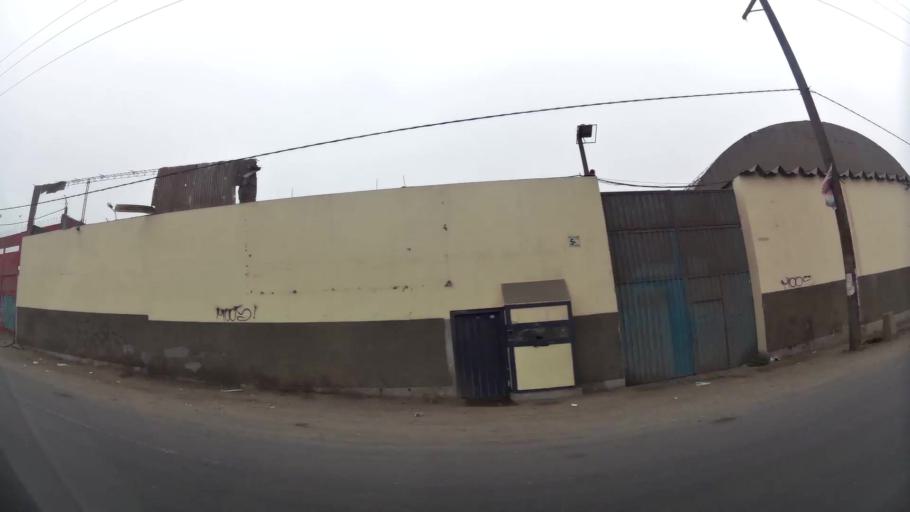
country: PE
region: Lima
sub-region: Lima
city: Santa Maria
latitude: -12.0137
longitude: -76.8825
